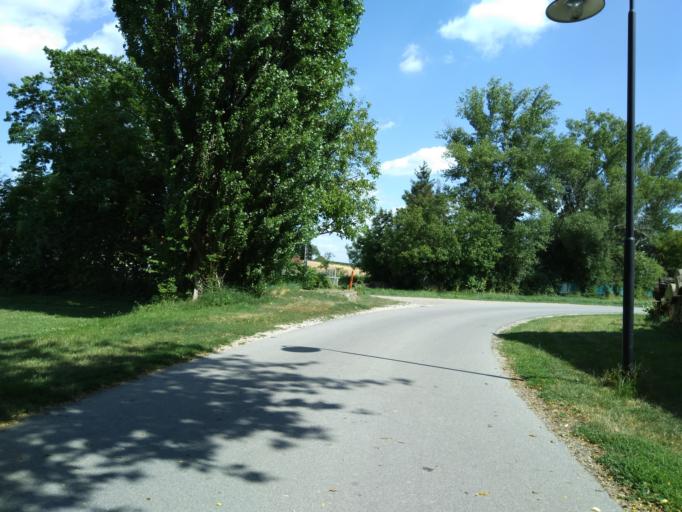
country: AT
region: Lower Austria
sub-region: Politischer Bezirk Mistelbach
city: Wolkersdorf im Weinviertel
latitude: 48.3724
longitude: 16.5246
